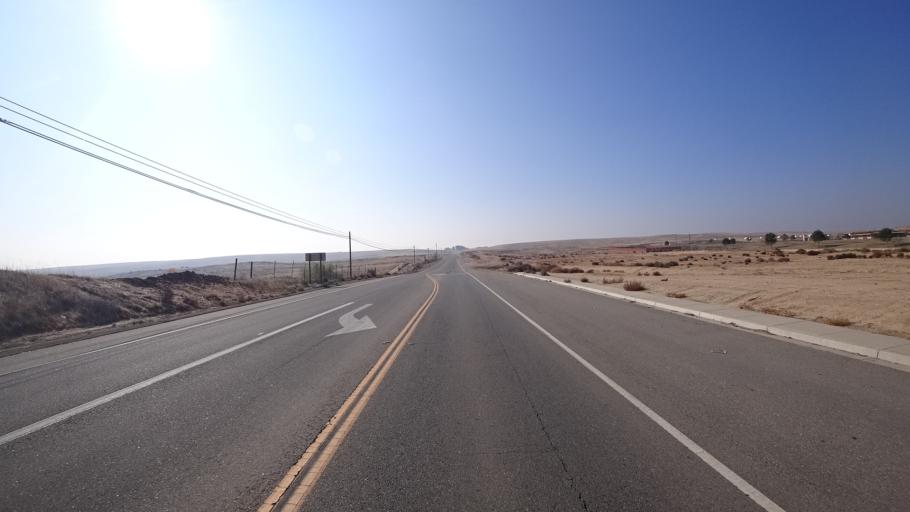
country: US
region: California
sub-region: Kern County
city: Bakersfield
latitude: 35.3892
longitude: -118.8908
